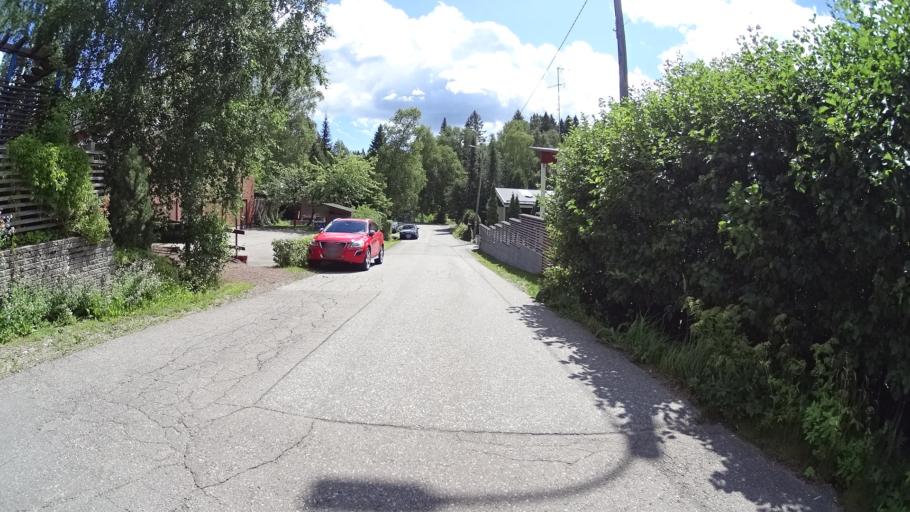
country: FI
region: Uusimaa
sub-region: Helsinki
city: Teekkarikylae
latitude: 60.2750
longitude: 24.8483
